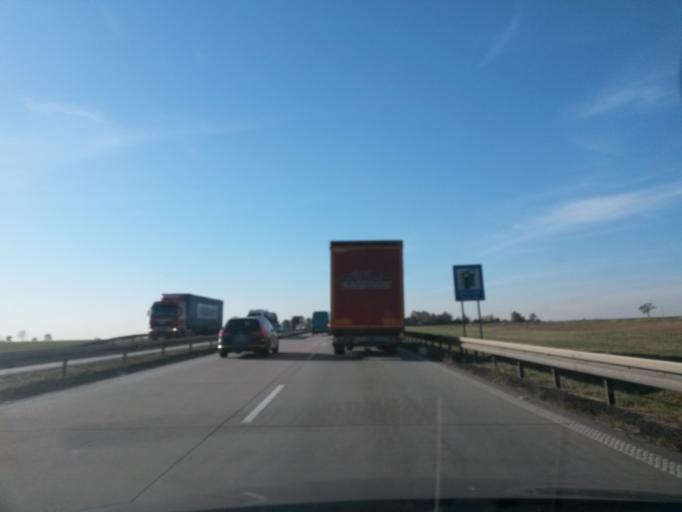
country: PL
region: Lower Silesian Voivodeship
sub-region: Powiat sredzki
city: Udanin
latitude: 51.0681
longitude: 16.4738
